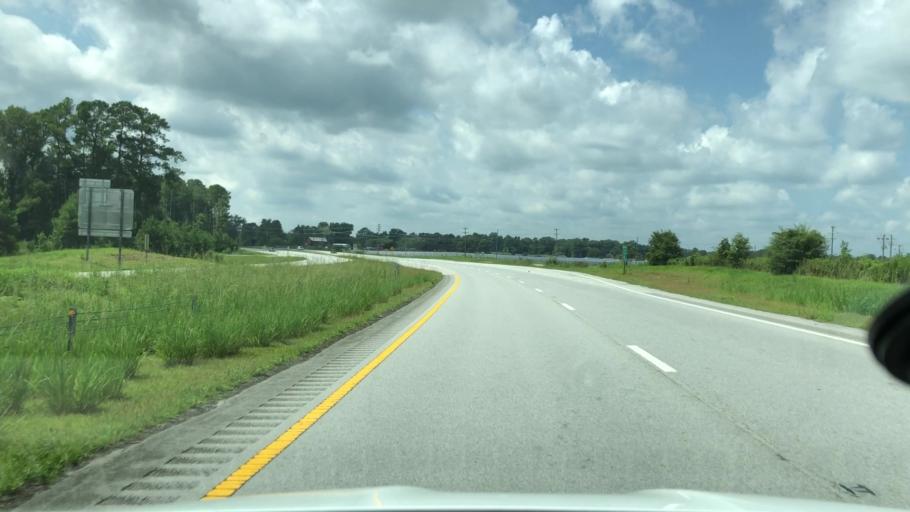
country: US
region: North Carolina
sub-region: Beaufort County
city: Washington
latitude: 35.5021
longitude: -77.1012
